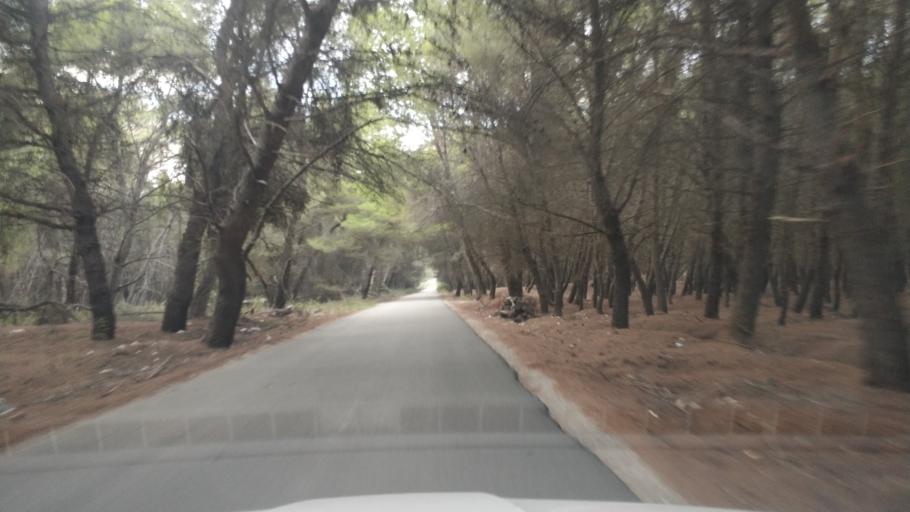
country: AL
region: Vlore
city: Vlore
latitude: 40.4986
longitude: 19.4307
